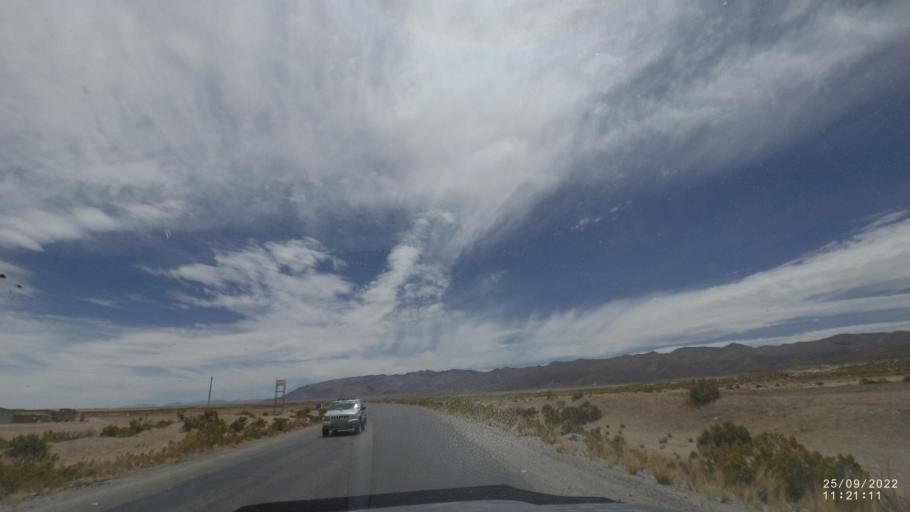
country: BO
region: Oruro
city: Challapata
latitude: -19.1475
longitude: -66.7715
